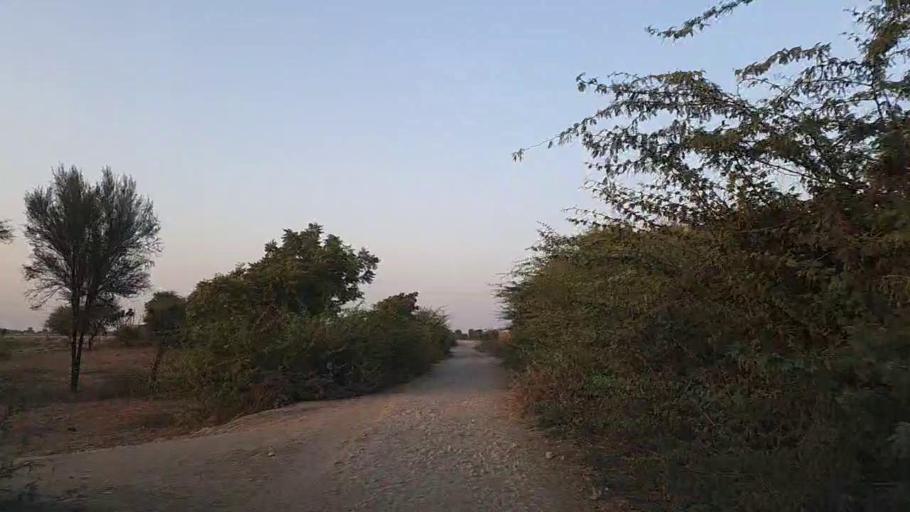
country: PK
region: Sindh
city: Naukot
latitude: 24.8836
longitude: 69.3537
